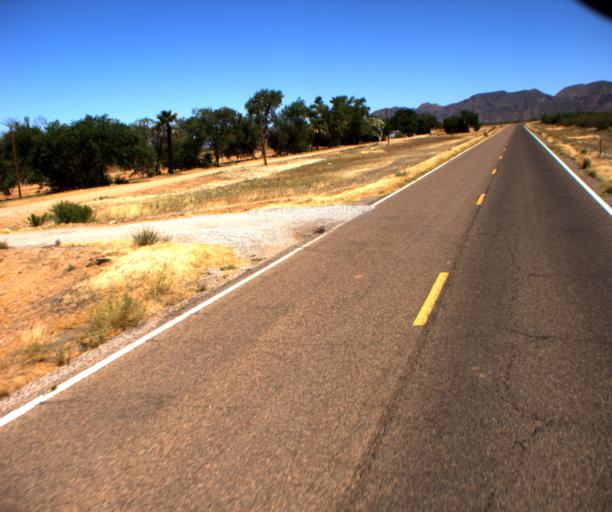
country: US
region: Arizona
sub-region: Yavapai County
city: Congress
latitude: 33.9683
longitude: -113.1415
